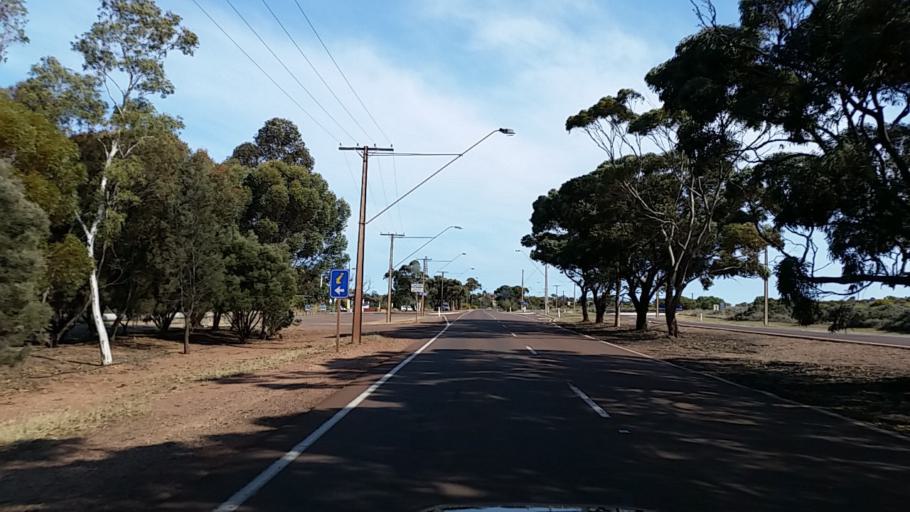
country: AU
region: South Australia
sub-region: Whyalla
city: Whyalla
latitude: -33.0177
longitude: 137.5749
